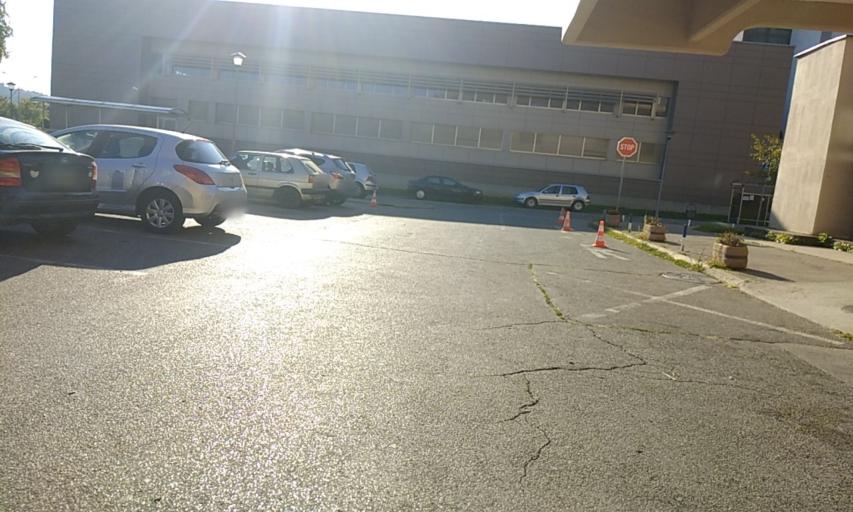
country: BA
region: Republika Srpska
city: Banja Luka
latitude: 44.7838
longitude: 17.1794
